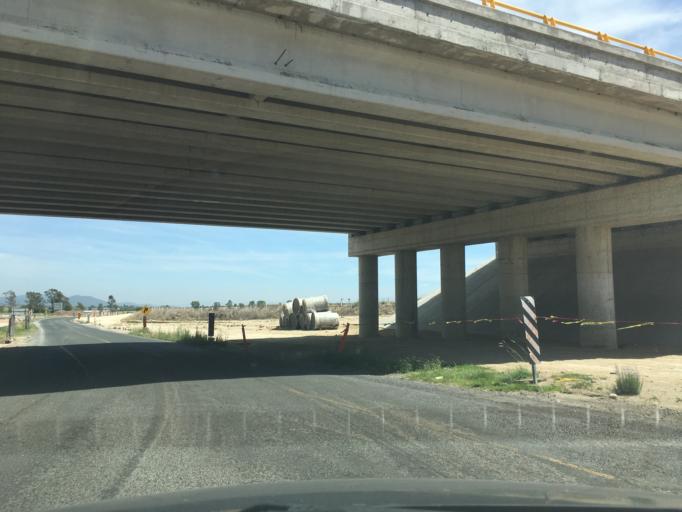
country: MX
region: Queretaro
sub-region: San Juan del Rio
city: El Jazmin
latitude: 20.2750
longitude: -100.0619
